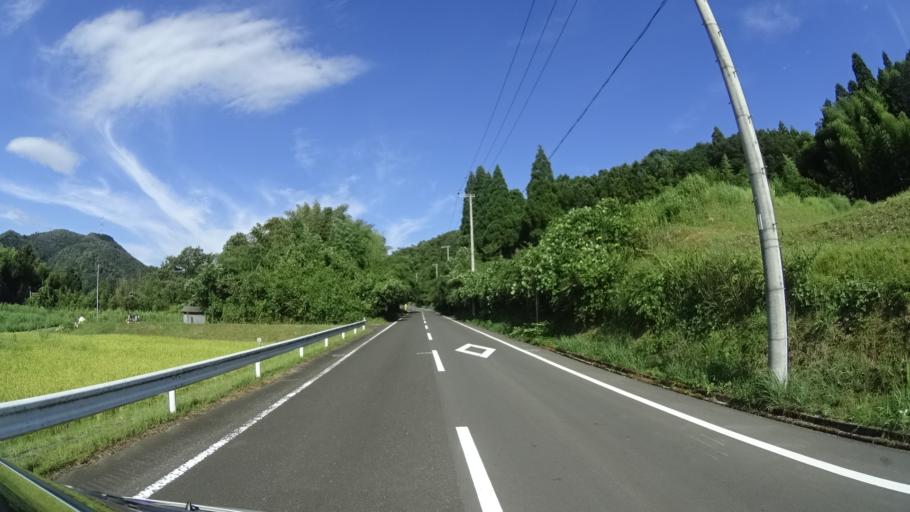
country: JP
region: Kyoto
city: Ayabe
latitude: 35.2861
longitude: 135.2941
